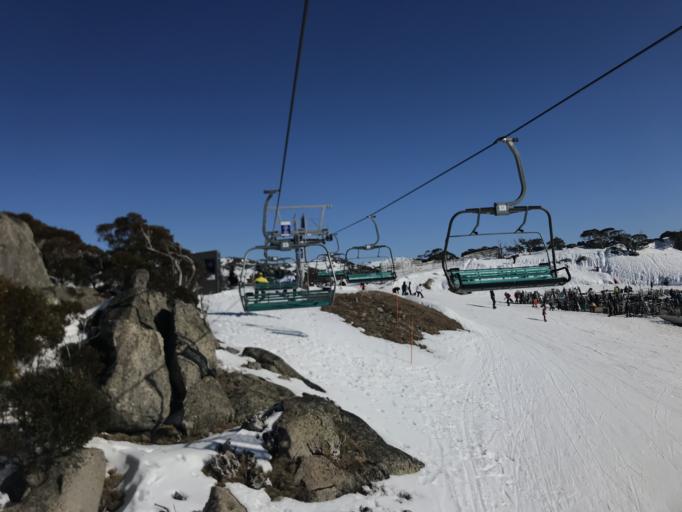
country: AU
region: New South Wales
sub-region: Snowy River
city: Jindabyne
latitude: -36.3863
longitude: 148.3939
